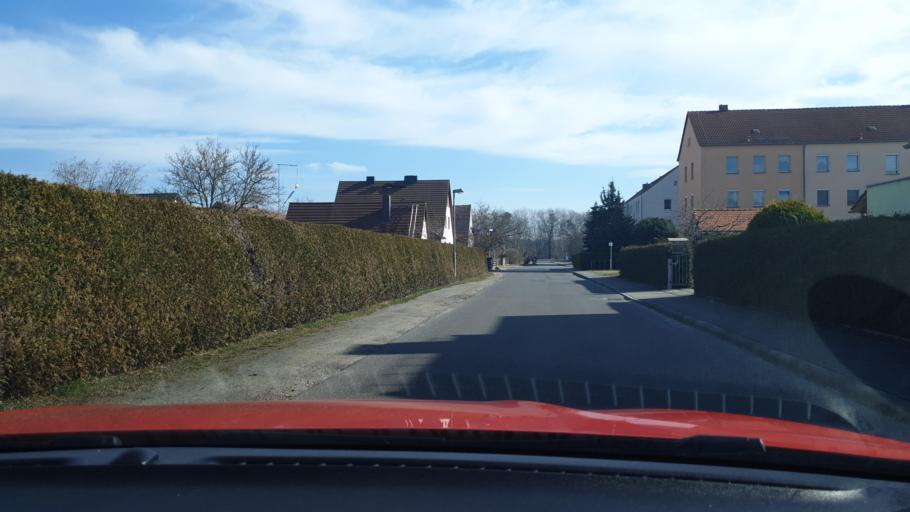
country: DE
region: Saxony
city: Ossling
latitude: 51.4474
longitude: 14.1296
